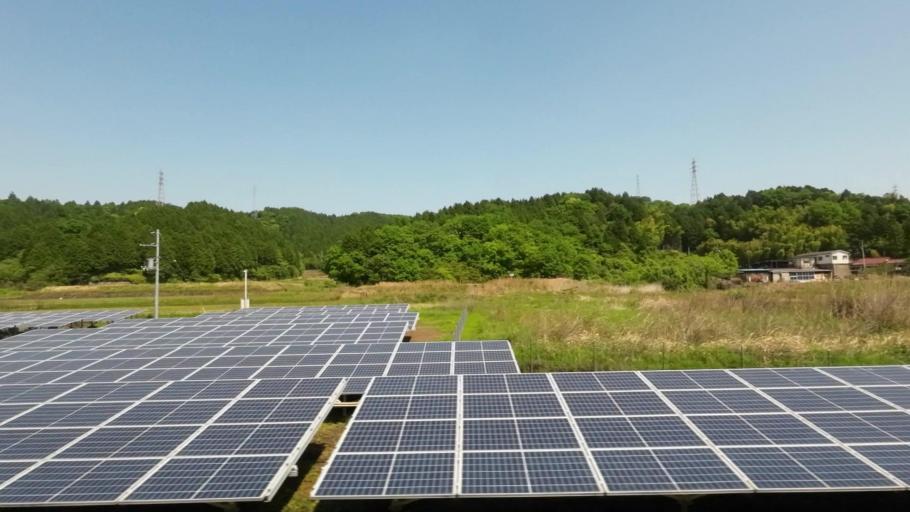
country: JP
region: Ehime
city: Niihama
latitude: 33.9276
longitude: 133.2576
